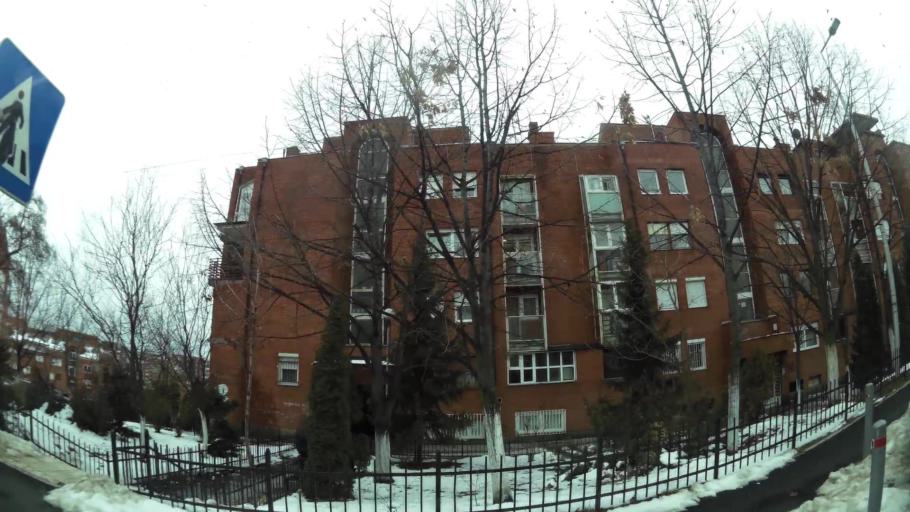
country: XK
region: Pristina
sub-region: Komuna e Prishtines
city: Pristina
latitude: 42.6492
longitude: 21.1699
